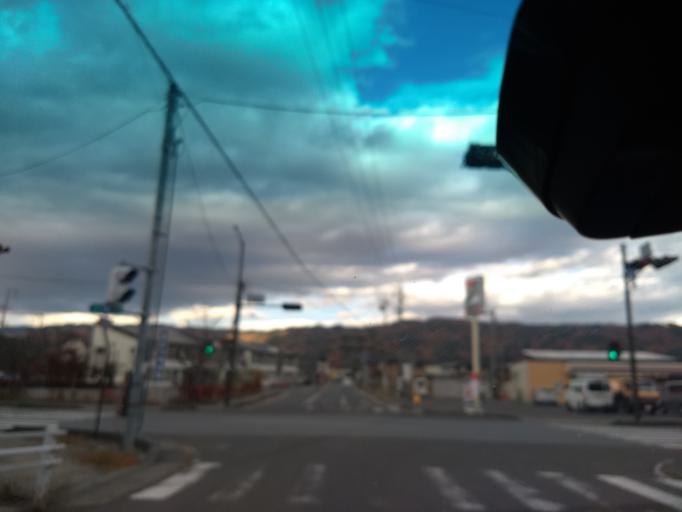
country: JP
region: Nagano
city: Chino
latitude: 35.9993
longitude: 138.1216
